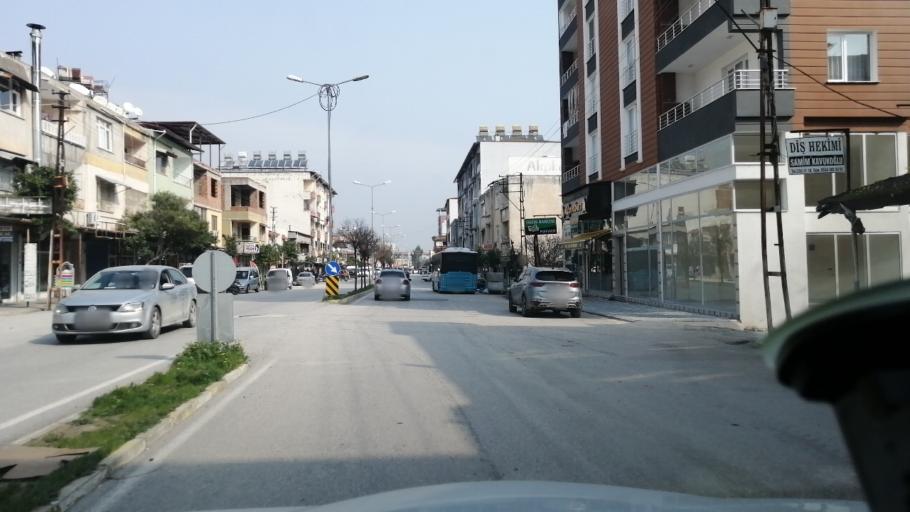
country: TR
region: Hatay
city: Serinyol
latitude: 36.3603
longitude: 36.2111
